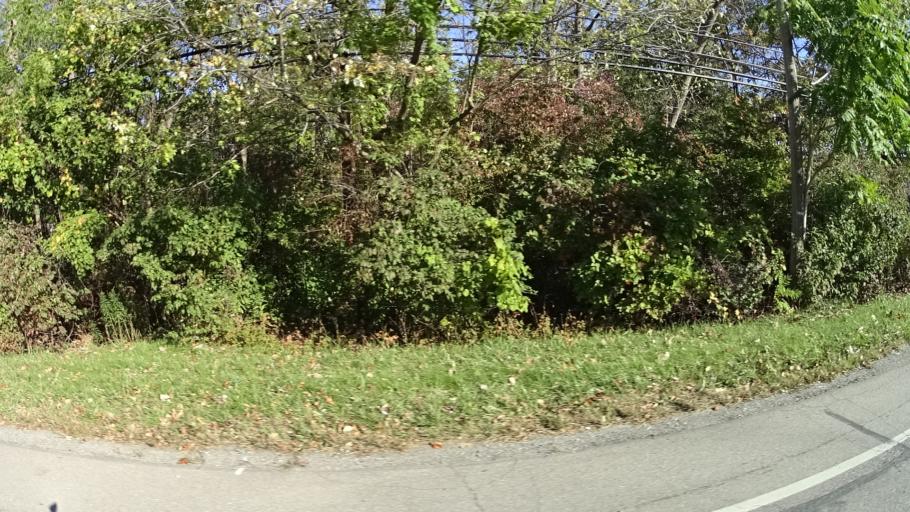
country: US
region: Ohio
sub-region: Lorain County
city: Vermilion-on-the-Lake
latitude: 41.4249
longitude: -82.3225
